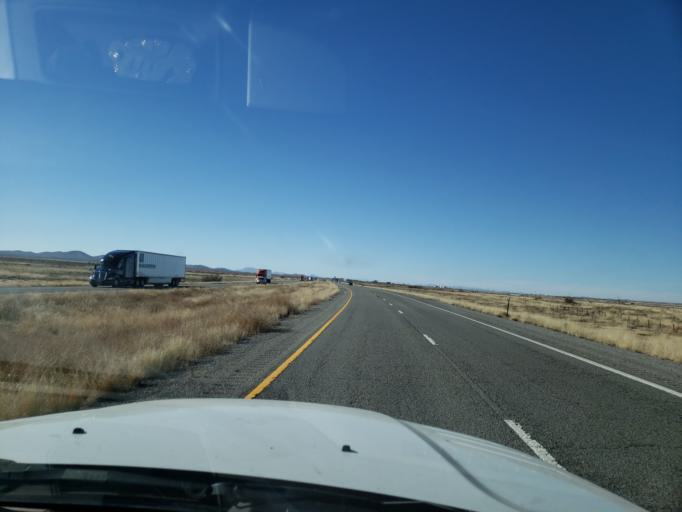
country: US
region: New Mexico
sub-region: Hidalgo County
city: Lordsburg
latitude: 32.3293
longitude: -108.6367
